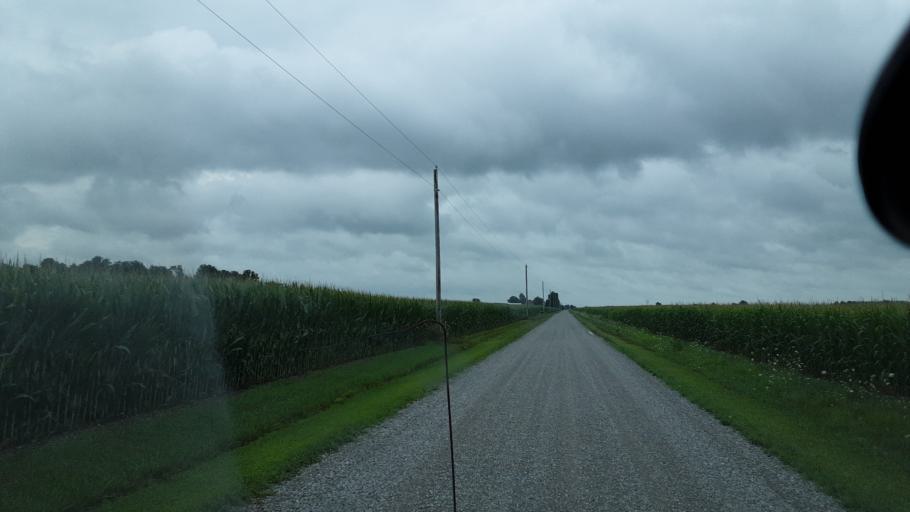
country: US
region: Indiana
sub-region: Wells County
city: Bluffton
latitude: 40.7844
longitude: -85.0716
